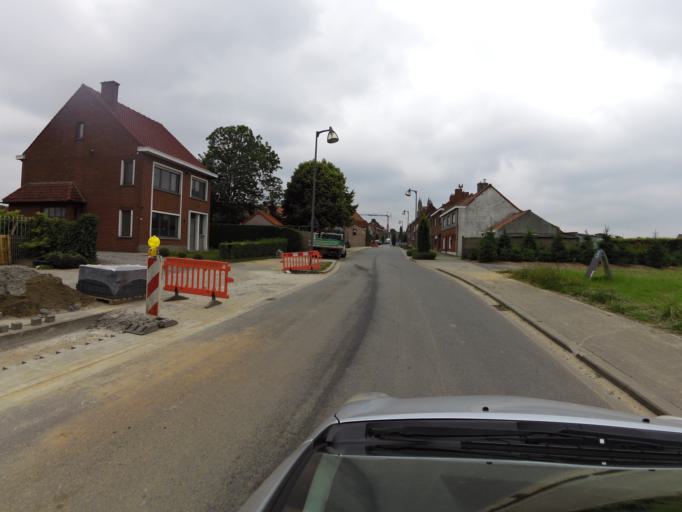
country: FR
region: Nord-Pas-de-Calais
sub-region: Departement du Nord
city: Saint-Jans-Cappel
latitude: 50.7800
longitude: 2.7731
